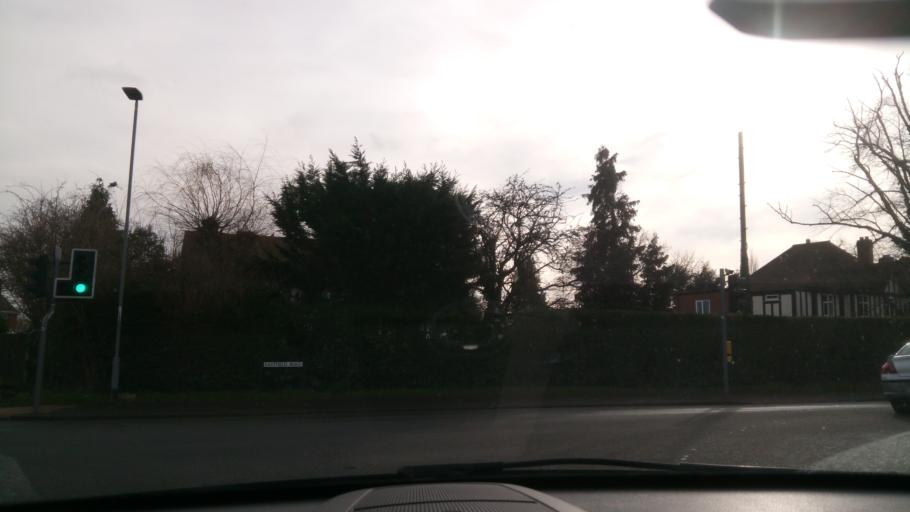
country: GB
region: England
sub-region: Peterborough
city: Peterborough
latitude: 52.5889
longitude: -0.2229
